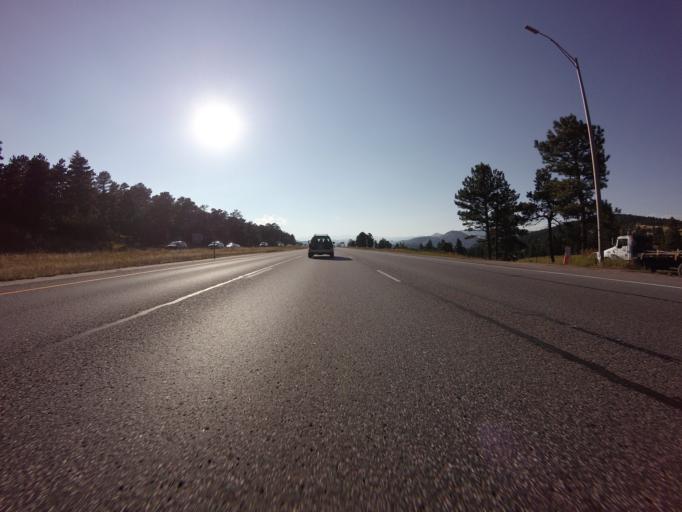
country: US
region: Colorado
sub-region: Jefferson County
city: Genesee
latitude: 39.7126
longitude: -105.3038
